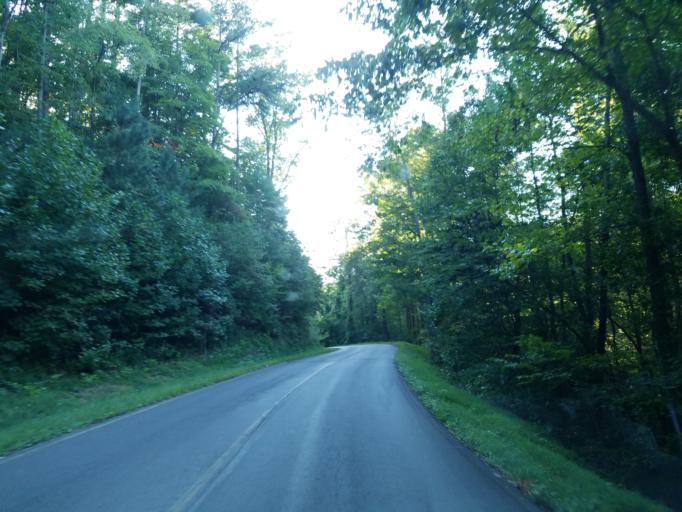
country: US
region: Georgia
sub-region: Murray County
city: Chatsworth
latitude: 34.9451
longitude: -84.7113
